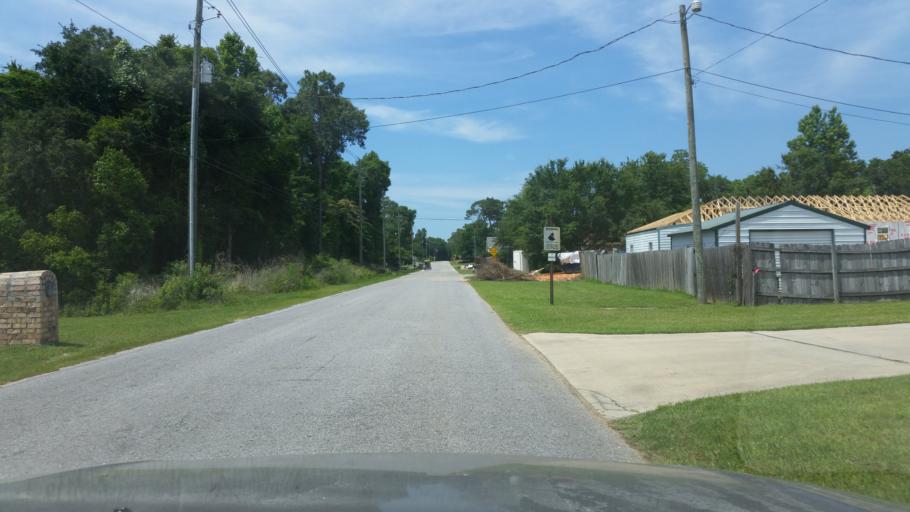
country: US
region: Florida
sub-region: Escambia County
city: Ferry Pass
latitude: 30.5347
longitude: -87.2267
